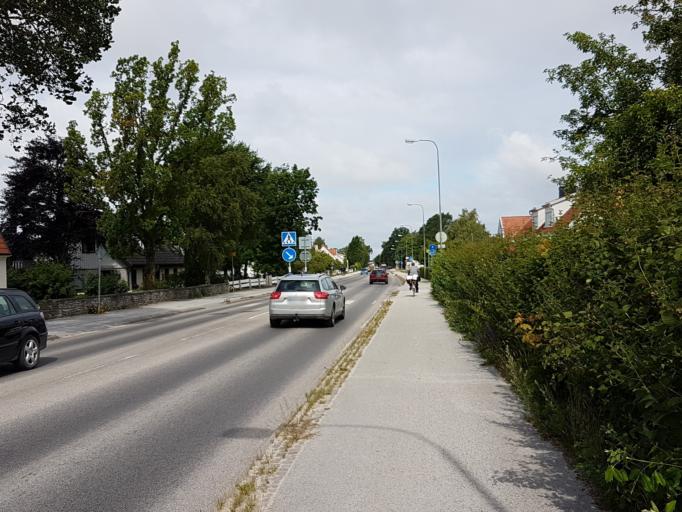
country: SE
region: Gotland
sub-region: Gotland
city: Visby
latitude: 57.6301
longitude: 18.3149
